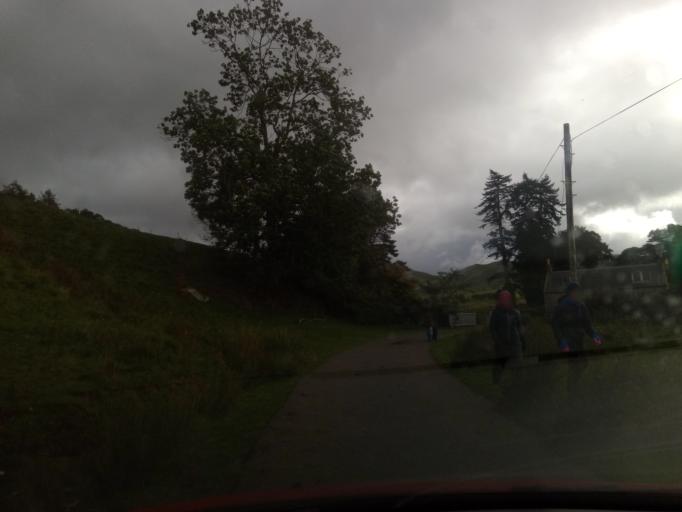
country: GB
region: Scotland
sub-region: The Scottish Borders
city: Coldstream
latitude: 55.5367
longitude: -2.2528
